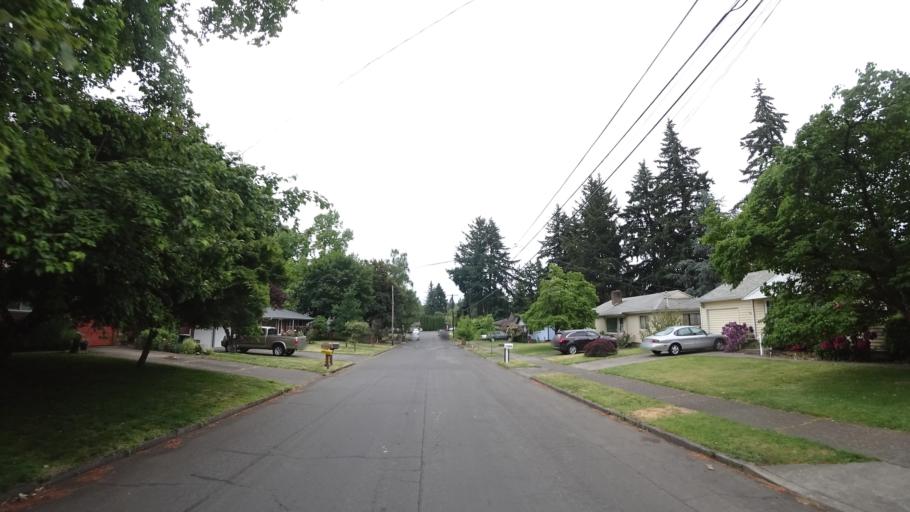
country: US
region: Oregon
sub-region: Multnomah County
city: Lents
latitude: 45.4981
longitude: -122.5435
